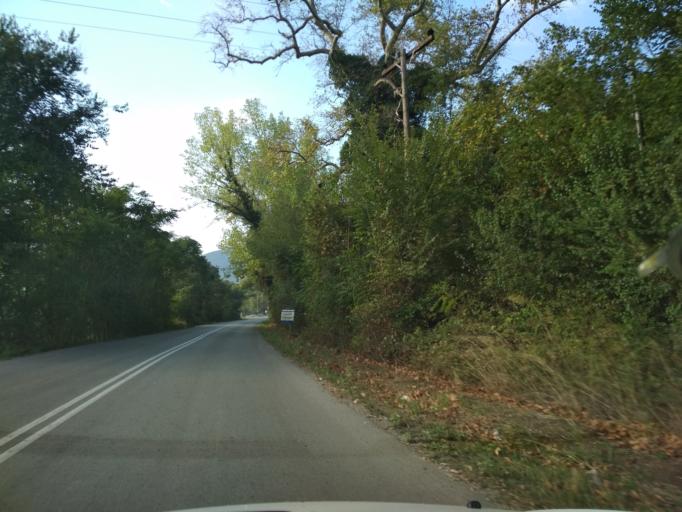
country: GR
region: Central Greece
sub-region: Nomos Evvoias
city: Prokopion
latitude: 38.7385
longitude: 23.4925
